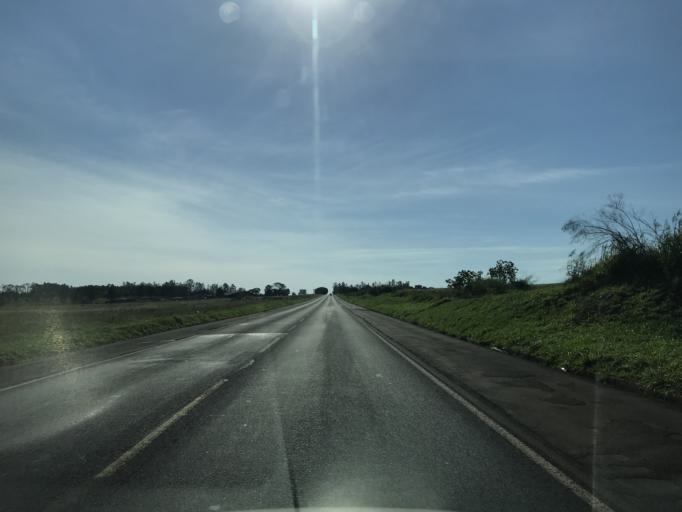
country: BR
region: Parana
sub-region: Umuarama
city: Umuarama
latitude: -23.8473
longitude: -53.3678
